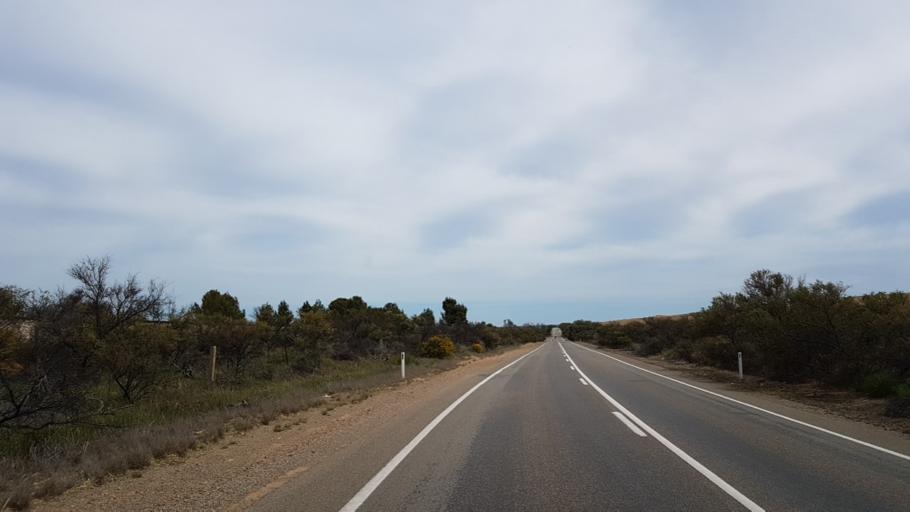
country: AU
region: South Australia
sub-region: Port Pirie City and Dists
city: Crystal Brook
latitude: -33.2353
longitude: 138.3904
